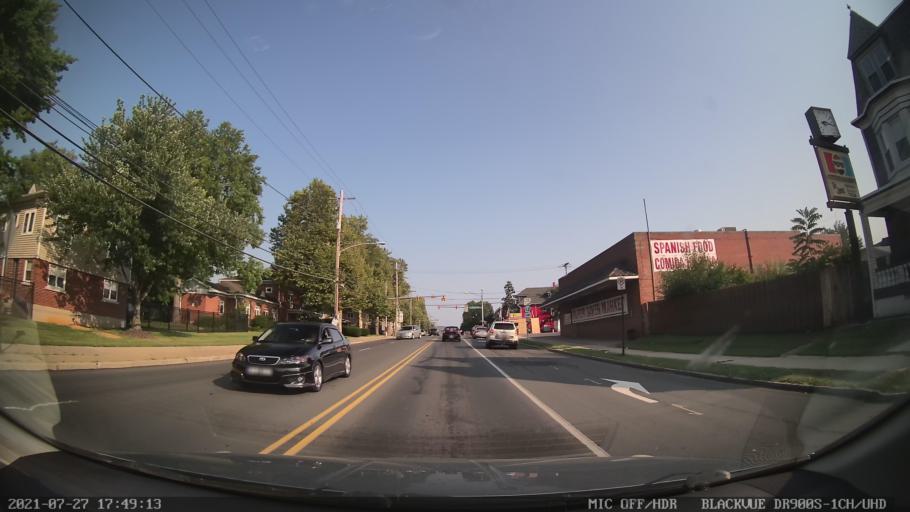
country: US
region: Pennsylvania
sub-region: Berks County
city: West Reading
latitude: 40.3552
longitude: -75.9481
